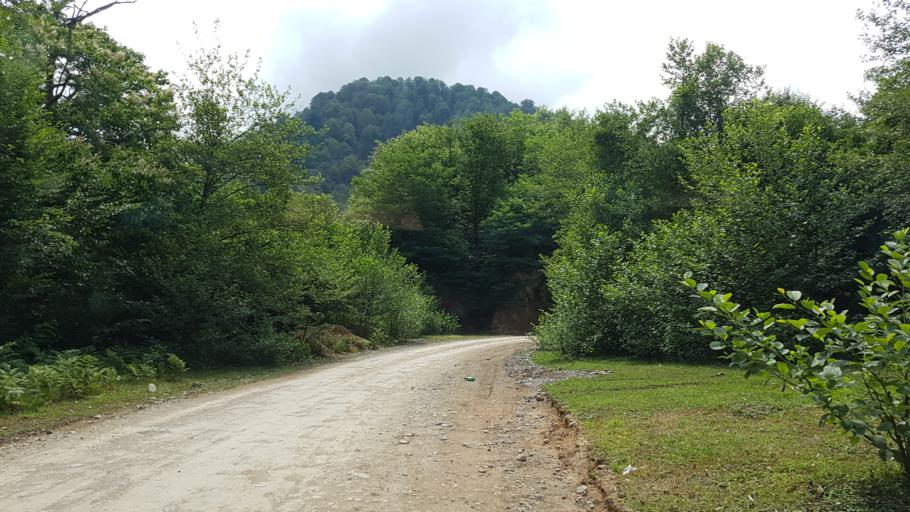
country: GE
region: Guria
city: Ozurgeti
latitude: 41.8649
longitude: 42.1115
